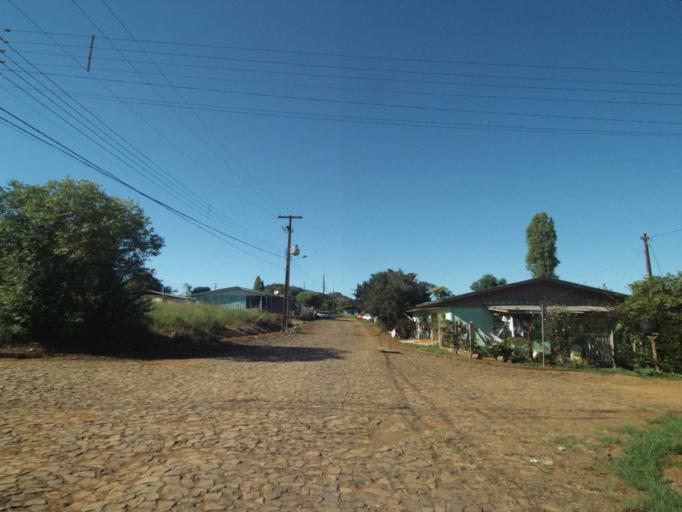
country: BR
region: Parana
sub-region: Pinhao
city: Pinhao
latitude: -25.8436
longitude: -52.0324
